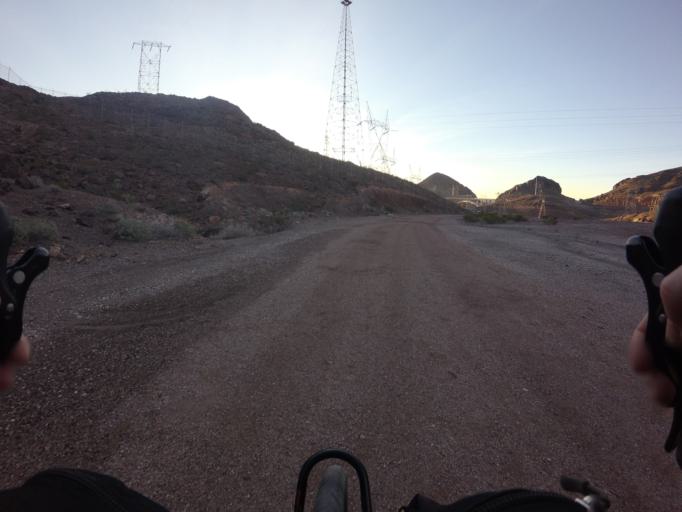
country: US
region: Nevada
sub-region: Clark County
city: Boulder City
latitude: 36.0196
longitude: -114.7458
